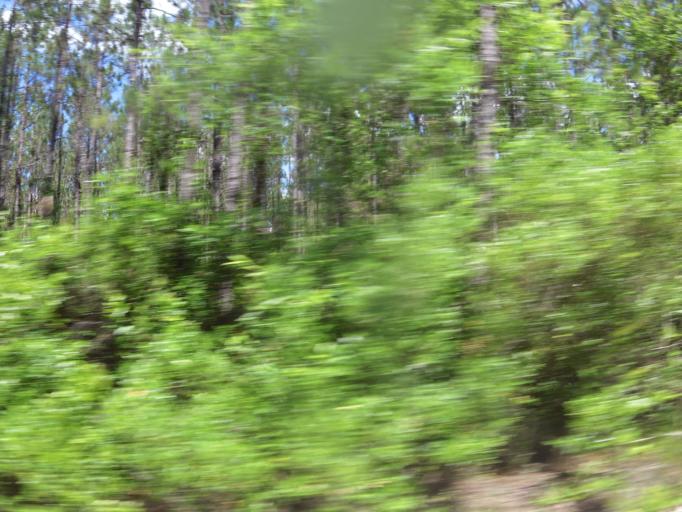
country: US
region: Florida
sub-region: Clay County
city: Asbury Lake
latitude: 29.8671
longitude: -81.8534
